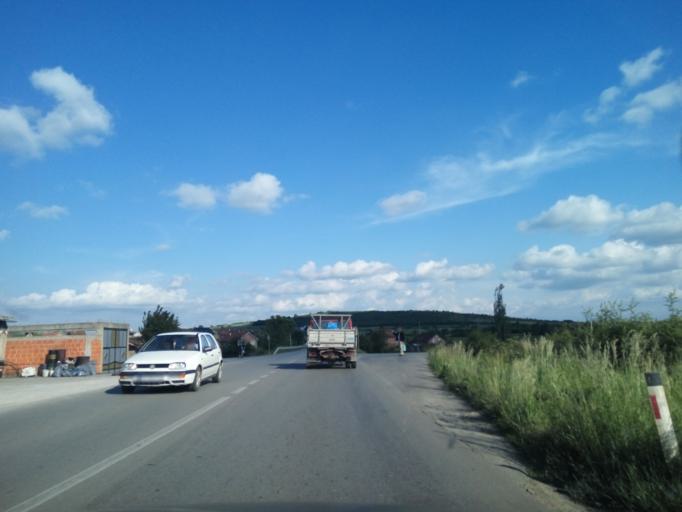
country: XK
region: Pec
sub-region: Komuna e Klines
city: Klina
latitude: 42.5920
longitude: 20.6628
